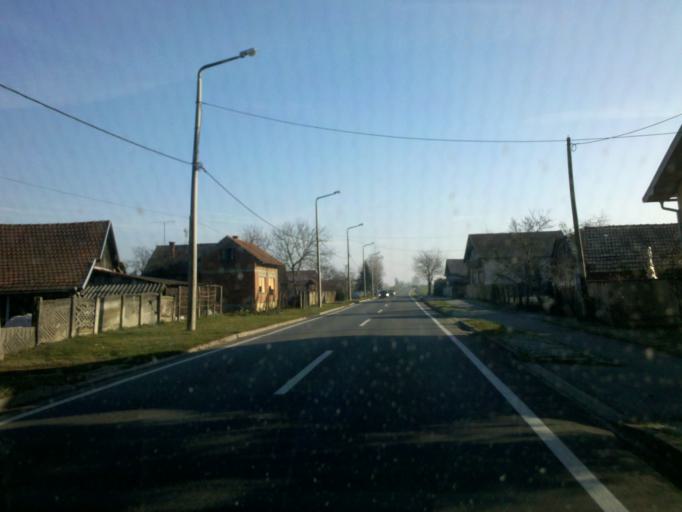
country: HR
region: Koprivnicko-Krizevacka
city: Virje
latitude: 46.0731
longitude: 16.9588
